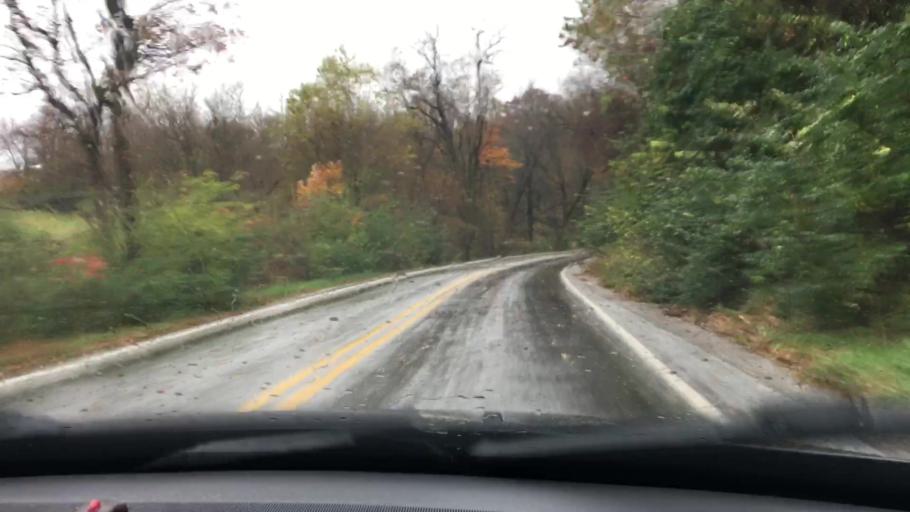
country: US
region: Pennsylvania
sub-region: York County
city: Susquehanna Trails
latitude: 39.7954
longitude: -76.4162
